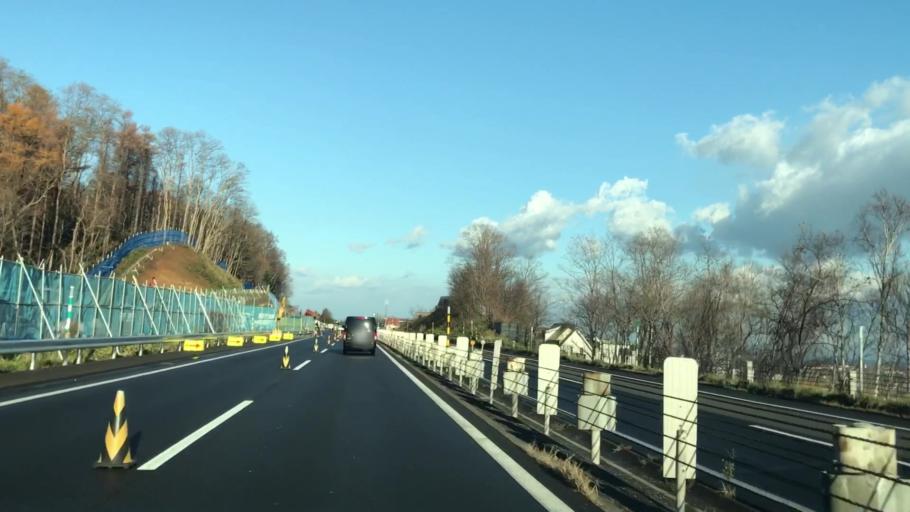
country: JP
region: Hokkaido
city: Sapporo
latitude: 43.1121
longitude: 141.2383
